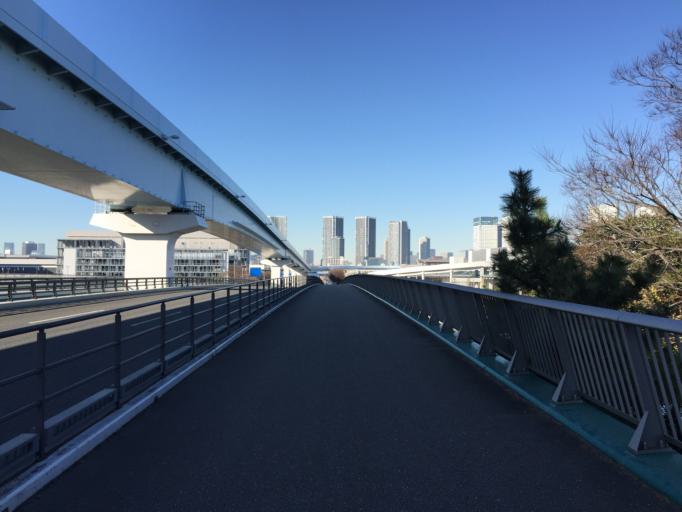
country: JP
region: Tokyo
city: Urayasu
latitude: 35.6418
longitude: 139.7876
